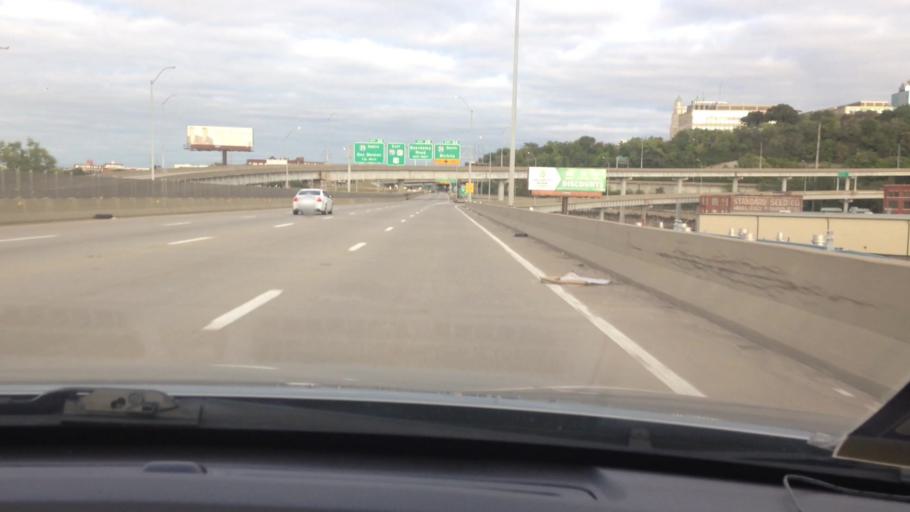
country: US
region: Missouri
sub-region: Jackson County
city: Kansas City
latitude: 39.1068
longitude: -94.5984
